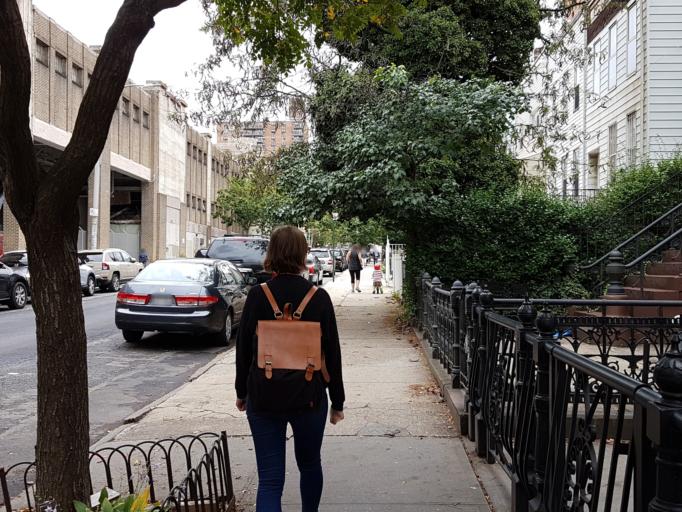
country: US
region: New York
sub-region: Kings County
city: Brooklyn
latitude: 40.6703
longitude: -73.9906
